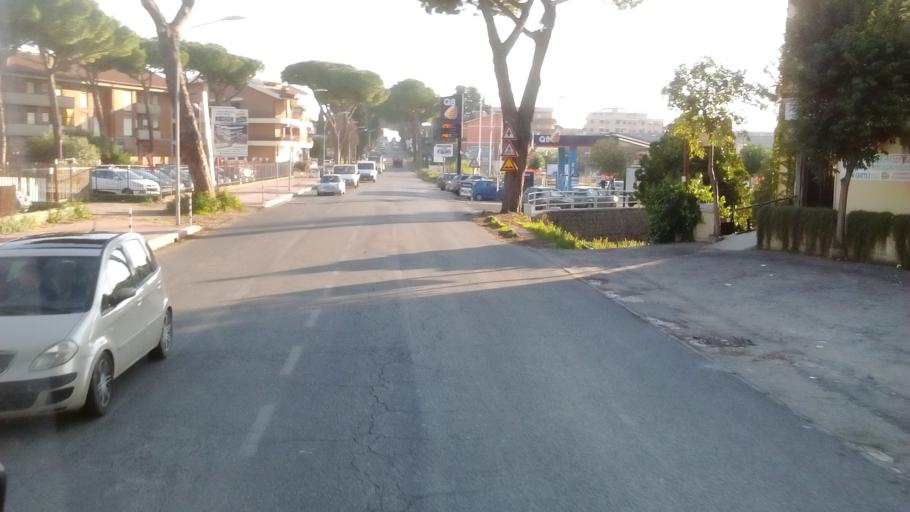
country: IT
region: Latium
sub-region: Citta metropolitana di Roma Capitale
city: Marino
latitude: 41.7658
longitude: 12.6163
